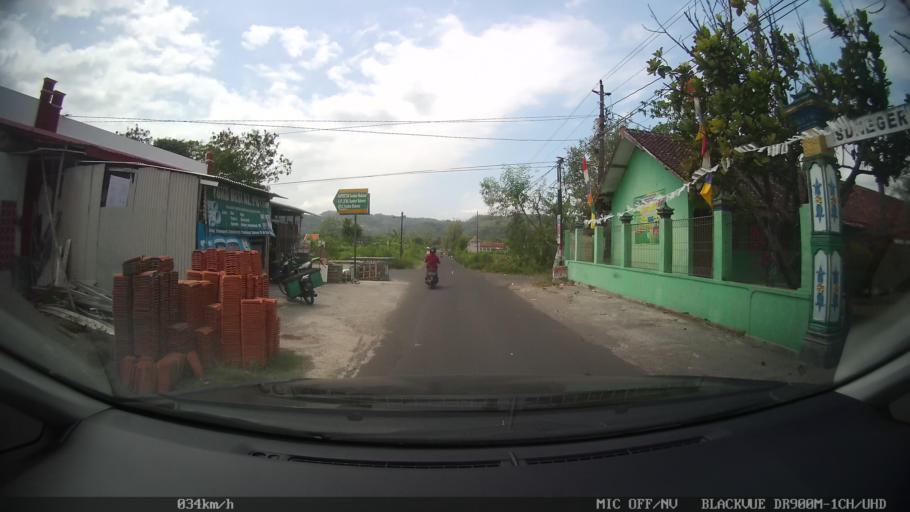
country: ID
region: Central Java
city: Candi Prambanan
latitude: -7.8124
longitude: 110.4906
